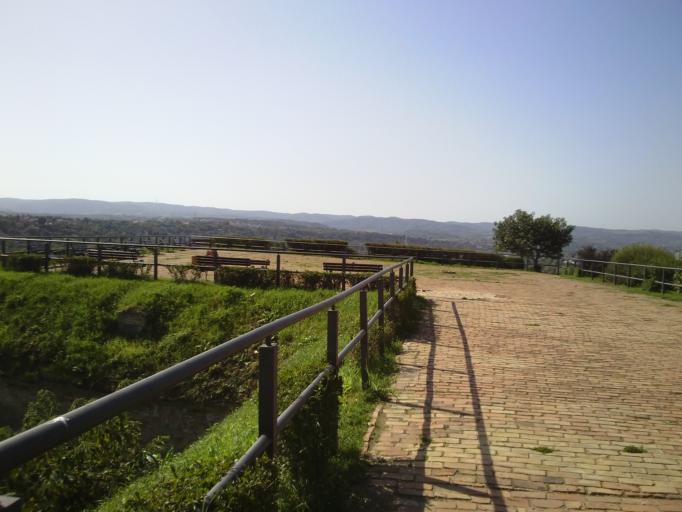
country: RS
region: Autonomna Pokrajina Vojvodina
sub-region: Juznobacki Okrug
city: Petrovaradin
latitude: 45.2510
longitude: 19.8631
